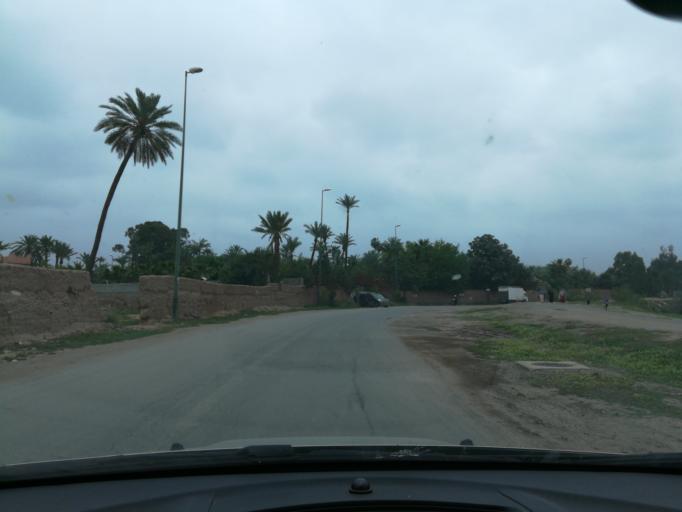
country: MA
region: Marrakech-Tensift-Al Haouz
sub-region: Marrakech
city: Marrakesh
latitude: 31.6609
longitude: -7.9830
